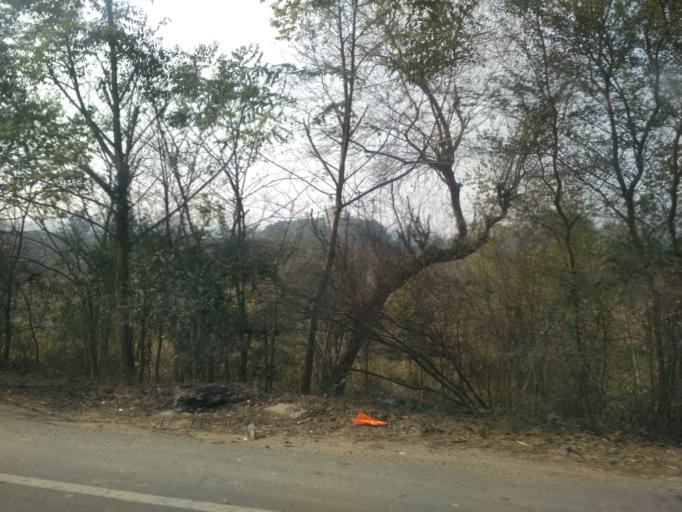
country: IN
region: Bihar
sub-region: Munger
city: Bariarpur
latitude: 25.4550
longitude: 86.6519
